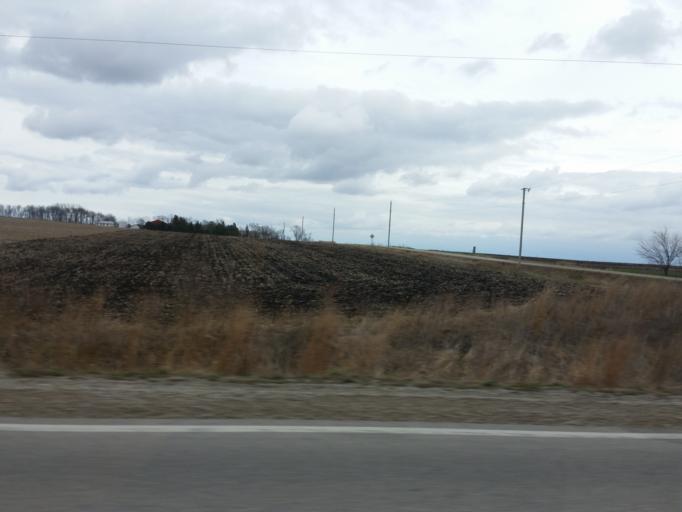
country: US
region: Iowa
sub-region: Black Hawk County
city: Elk Run Heights
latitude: 42.5128
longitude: -92.2195
